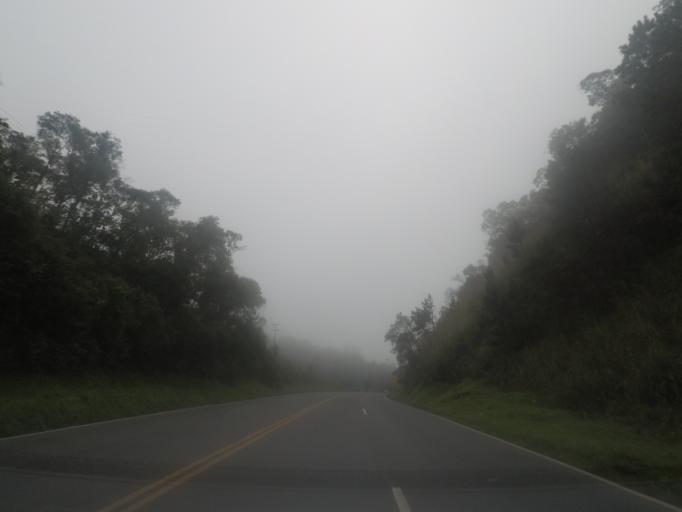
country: BR
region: Parana
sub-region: Almirante Tamandare
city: Almirante Tamandare
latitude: -25.2774
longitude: -49.3035
